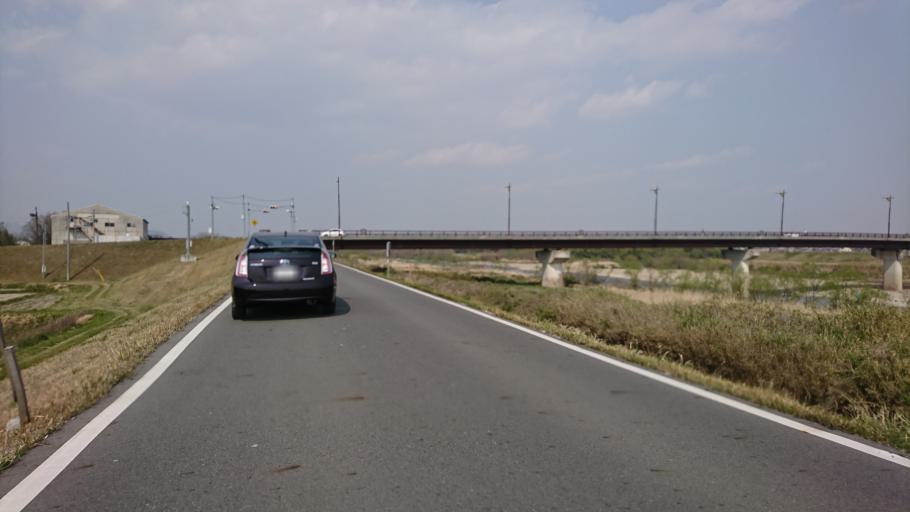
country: JP
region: Hyogo
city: Ono
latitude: 34.8771
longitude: 134.9252
